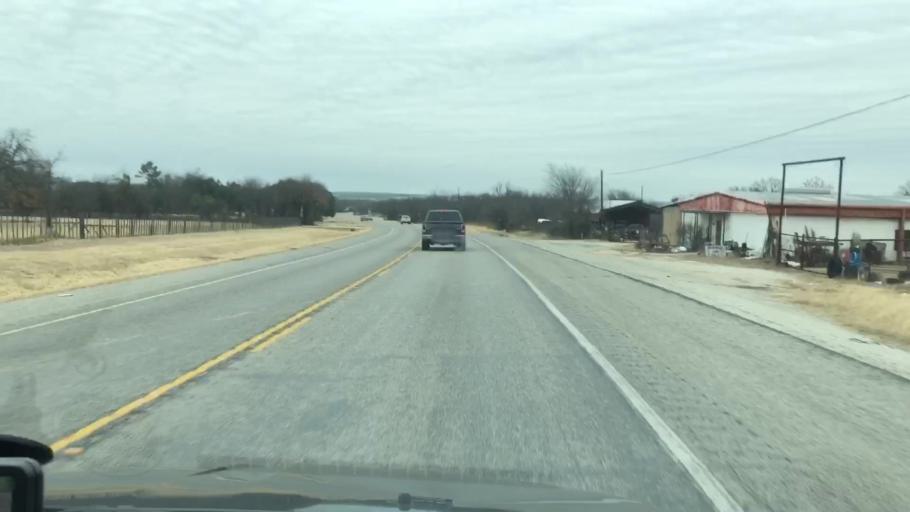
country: US
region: Texas
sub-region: Palo Pinto County
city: Mineral Wells
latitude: 32.8845
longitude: -98.0892
